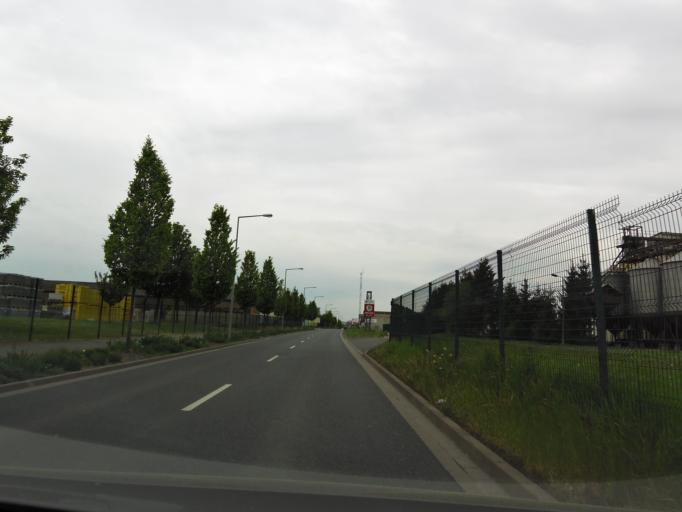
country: DE
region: Thuringia
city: Gotha
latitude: 50.9500
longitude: 10.7274
